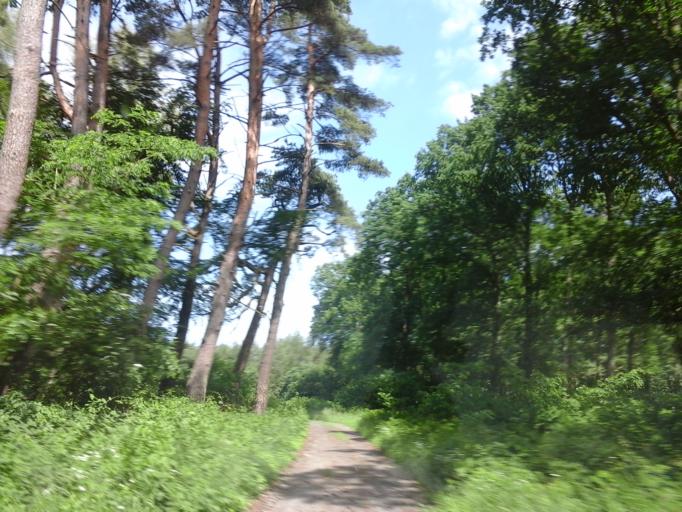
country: PL
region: West Pomeranian Voivodeship
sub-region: Powiat stargardzki
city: Dolice
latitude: 53.2221
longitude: 15.2494
